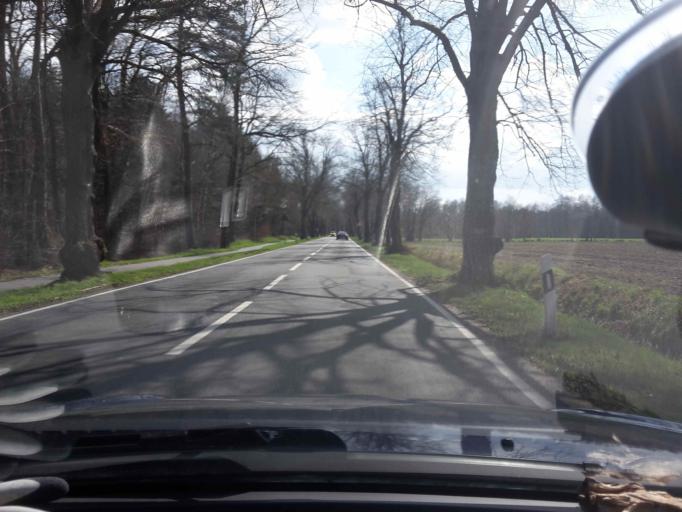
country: DE
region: Lower Saxony
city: Asendorf
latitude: 53.2865
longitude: 10.0016
